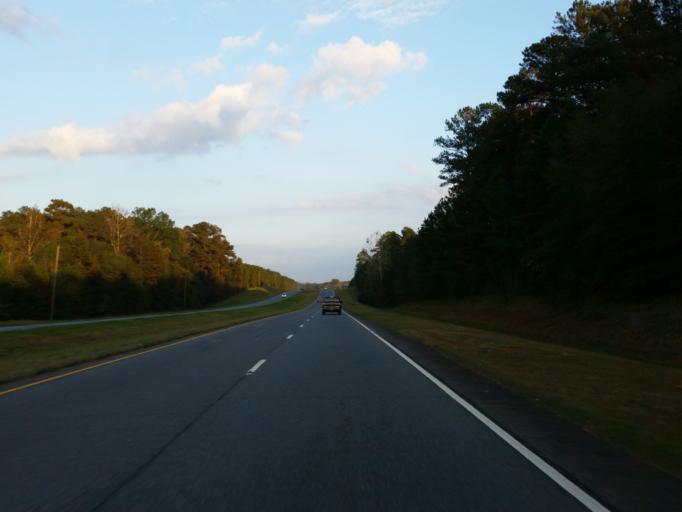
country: US
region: Georgia
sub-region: Houston County
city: Perry
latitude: 32.4129
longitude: -83.6652
